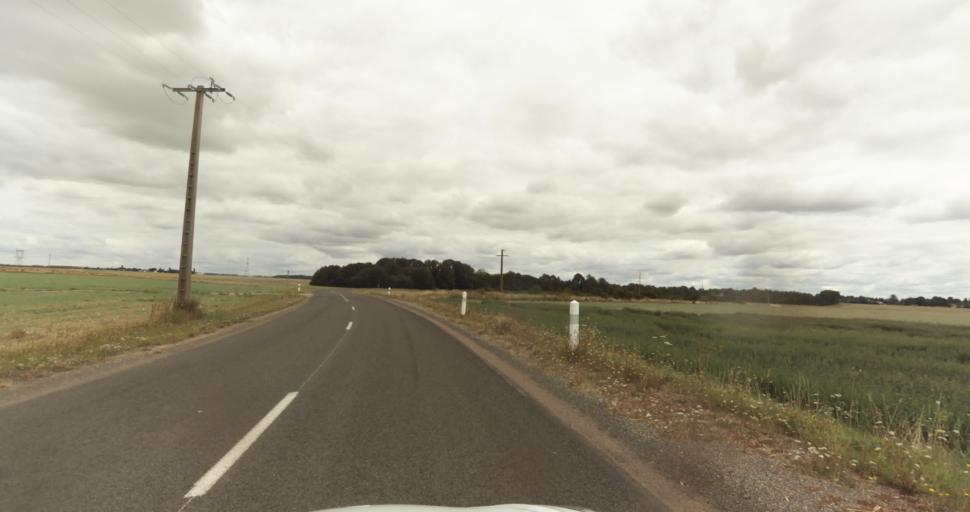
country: FR
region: Haute-Normandie
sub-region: Departement de l'Eure
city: La Madeleine-de-Nonancourt
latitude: 48.8343
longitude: 1.2296
